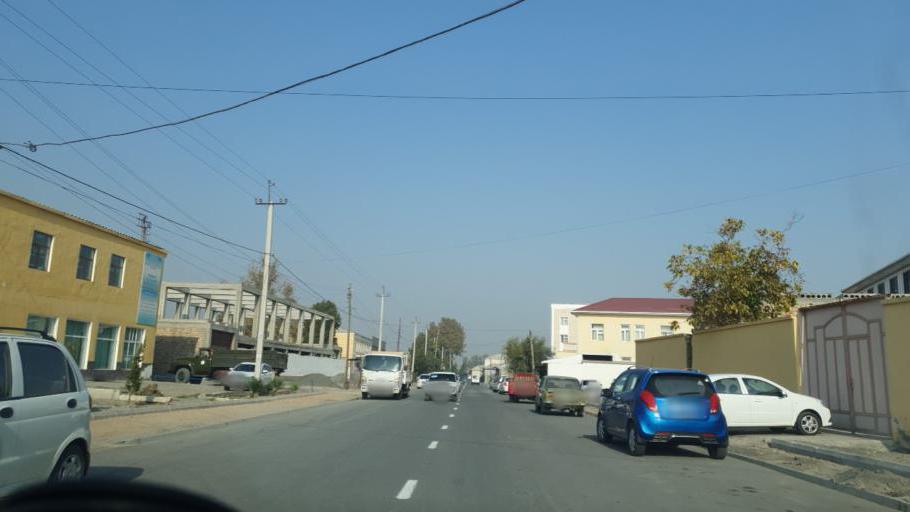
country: UZ
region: Fergana
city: Qo`qon
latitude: 40.5785
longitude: 70.9147
